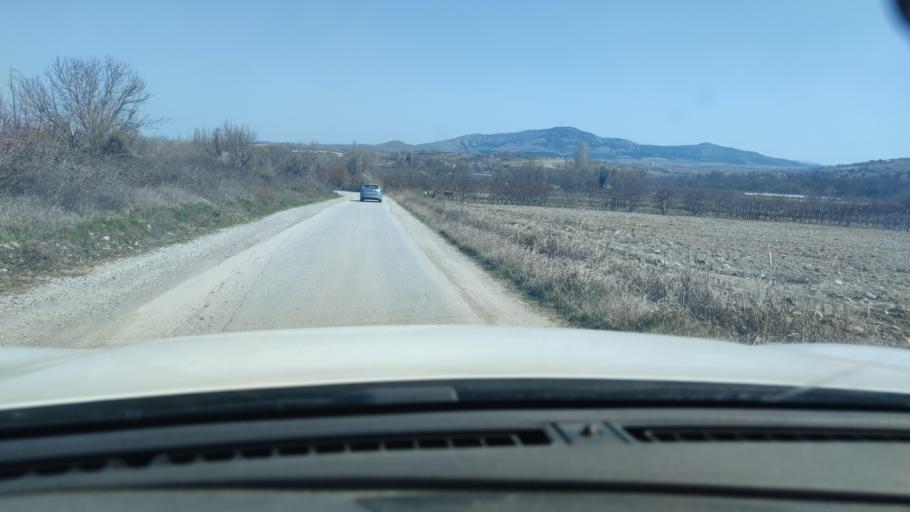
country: MK
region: Rosoman
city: Rosoman
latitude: 41.4748
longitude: 21.9074
